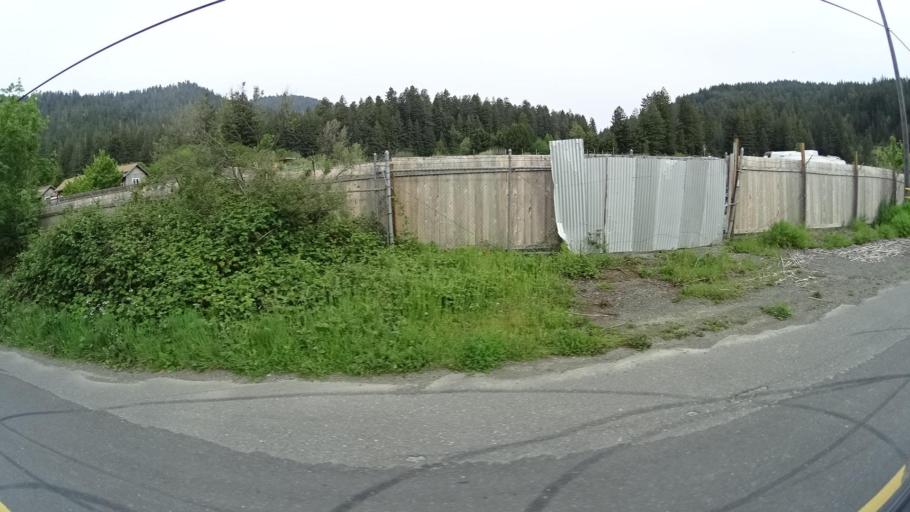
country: US
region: California
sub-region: Humboldt County
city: Redway
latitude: 40.2645
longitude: -123.8740
